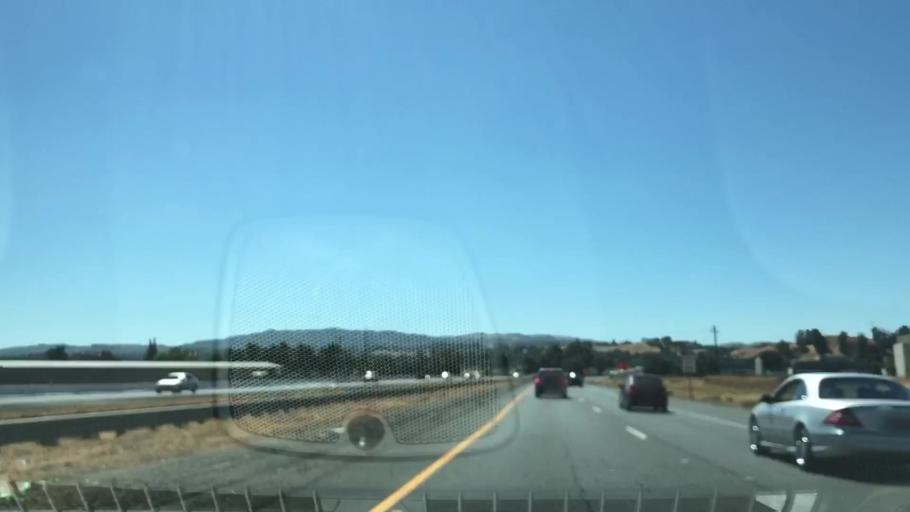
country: US
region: California
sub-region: Contra Costa County
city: Pacheco
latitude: 37.9984
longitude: -122.0607
